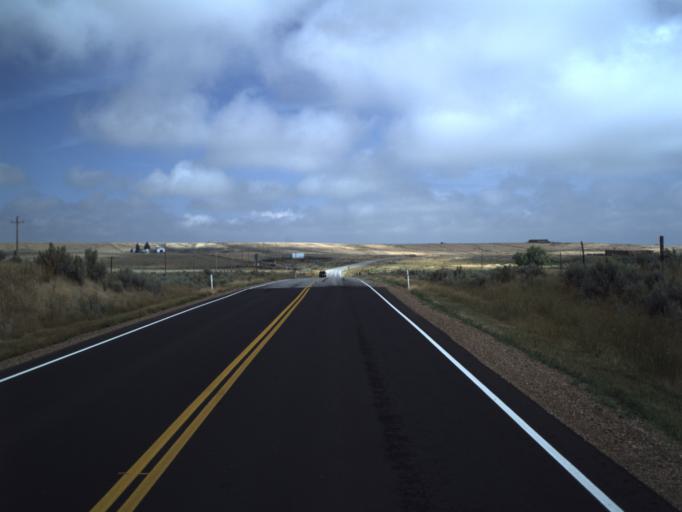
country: US
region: Utah
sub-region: Rich County
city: Randolph
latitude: 41.6902
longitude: -111.1761
